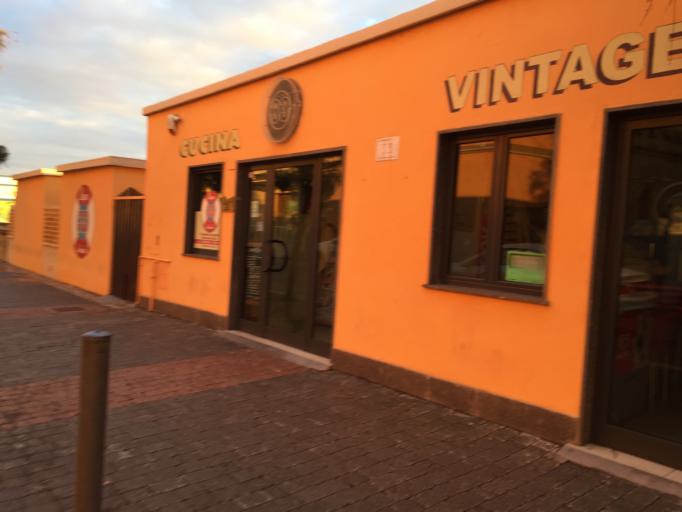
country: IT
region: Latium
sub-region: Citta metropolitana di Roma Capitale
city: Ladispoli
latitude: 41.9479
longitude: 12.0761
